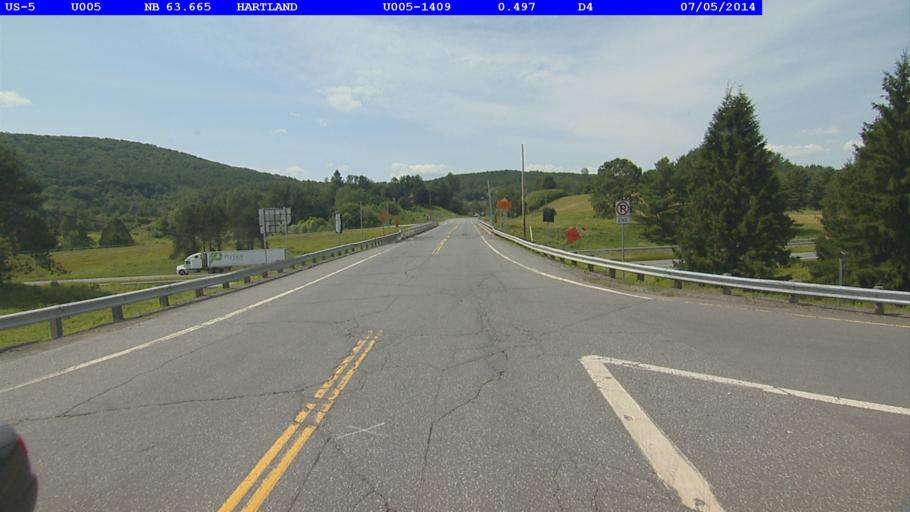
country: US
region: Vermont
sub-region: Windsor County
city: Windsor
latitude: 43.5268
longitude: -72.4013
